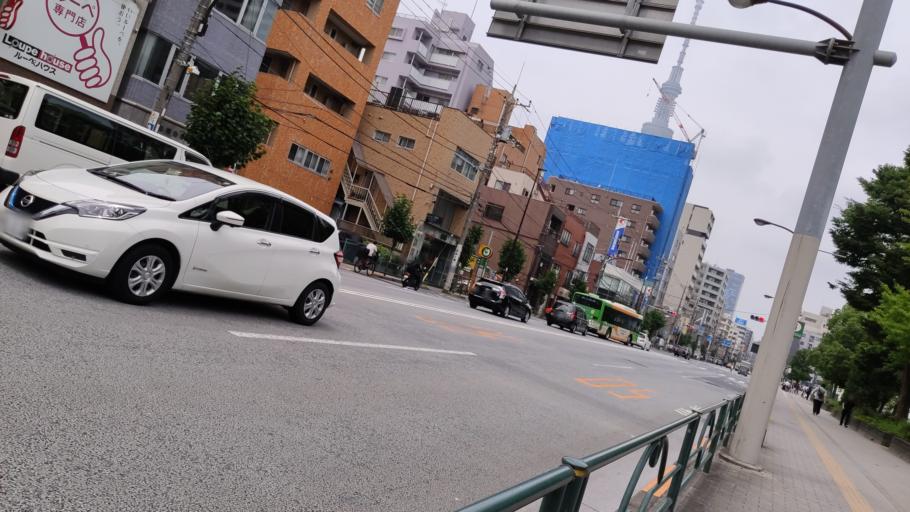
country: JP
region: Tokyo
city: Urayasu
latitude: 35.6991
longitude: 139.8148
